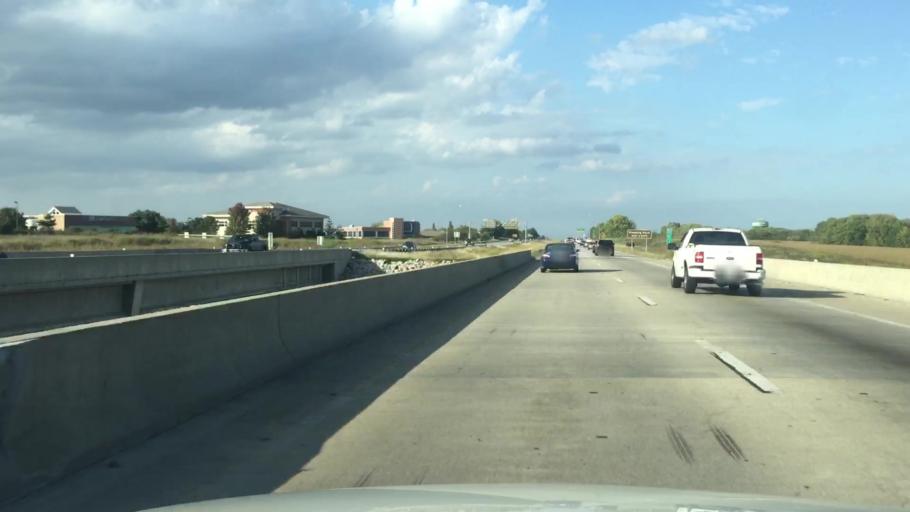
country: US
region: Missouri
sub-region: Jackson County
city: Lees Summit
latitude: 38.9678
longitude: -94.3580
